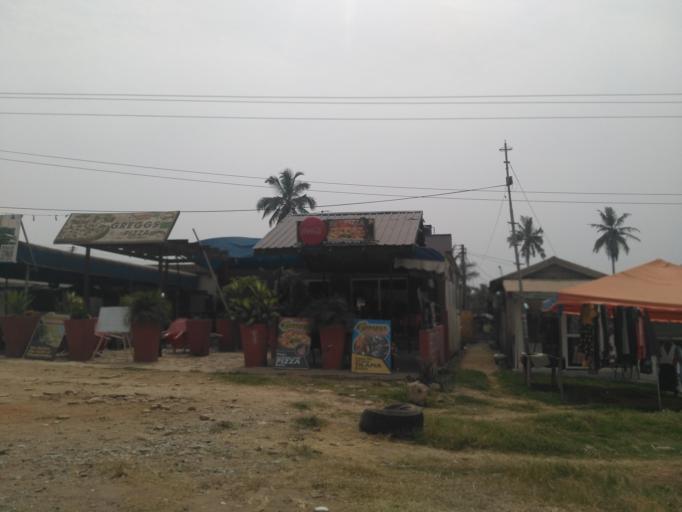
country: GH
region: Greater Accra
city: Nungua
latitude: 5.5930
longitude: -0.0903
